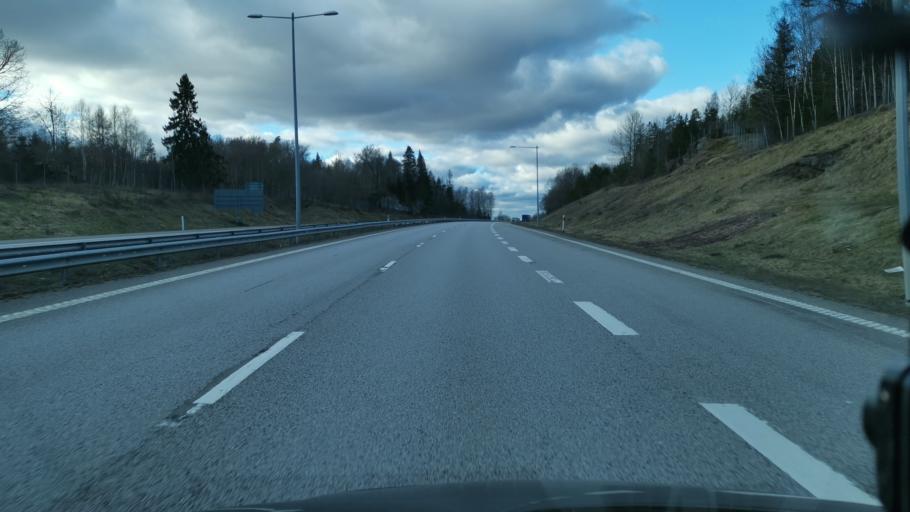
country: SE
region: Vaestra Goetaland
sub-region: Uddevalla Kommun
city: Ljungskile
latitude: 58.2938
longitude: 11.8655
